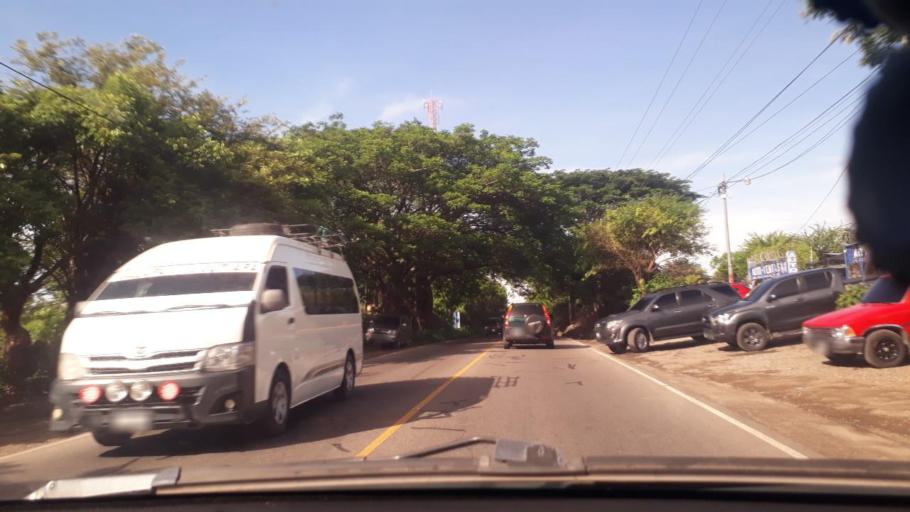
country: GT
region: Jutiapa
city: El Progreso
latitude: 14.3210
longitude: -89.8631
